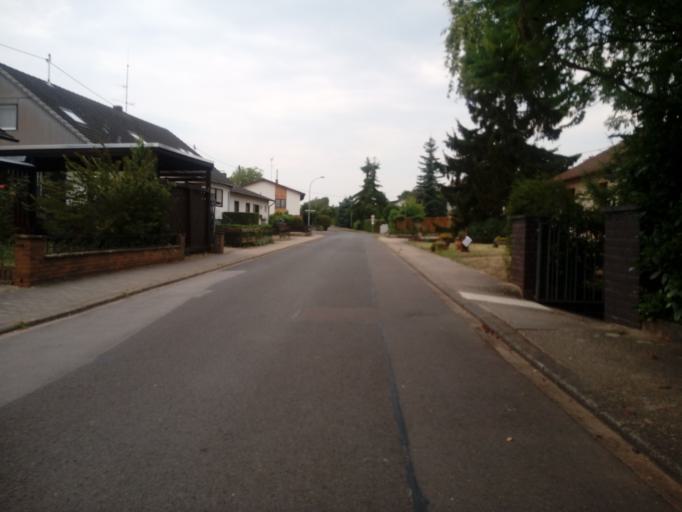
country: DE
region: Rheinland-Pfalz
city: Gutenberg
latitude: 49.8800
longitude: 7.7958
